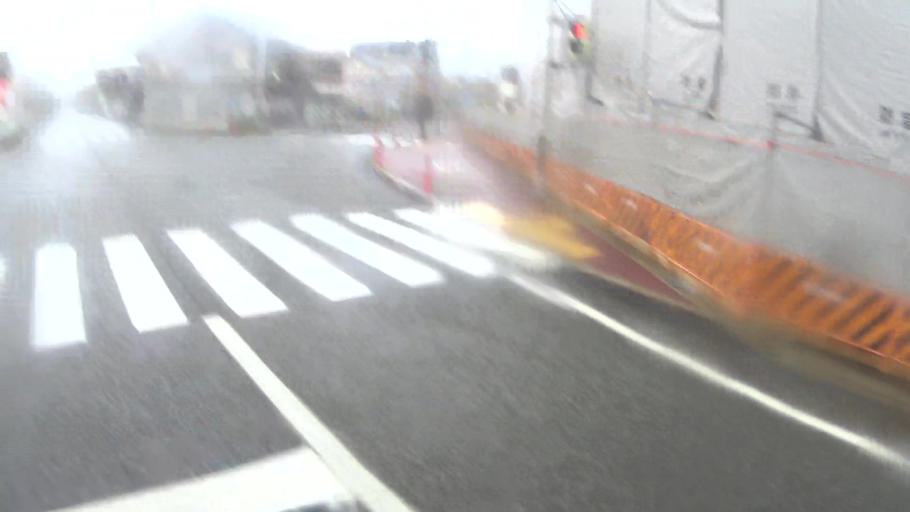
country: JP
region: Kyoto
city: Ayabe
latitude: 35.2991
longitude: 135.2522
